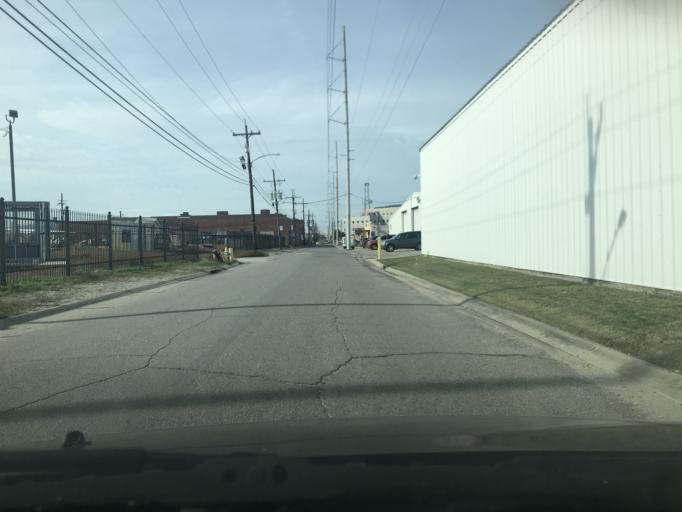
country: US
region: Louisiana
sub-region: Orleans Parish
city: New Orleans
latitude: 29.9581
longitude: -90.0994
